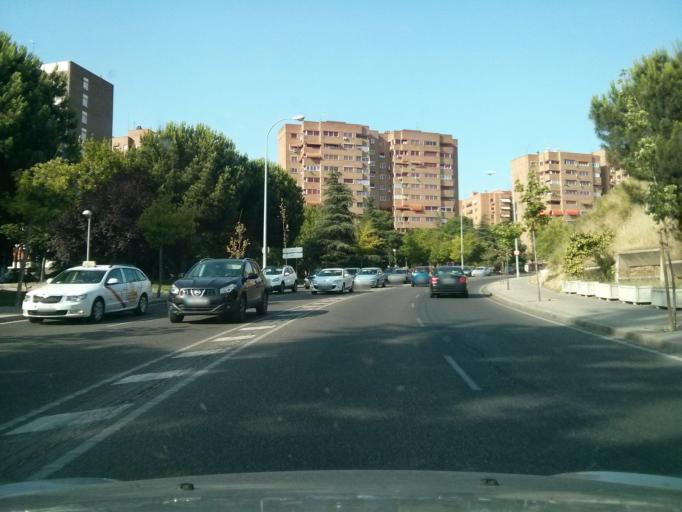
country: ES
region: Madrid
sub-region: Provincia de Madrid
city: Tetuan de las Victorias
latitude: 40.4744
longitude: -3.7012
